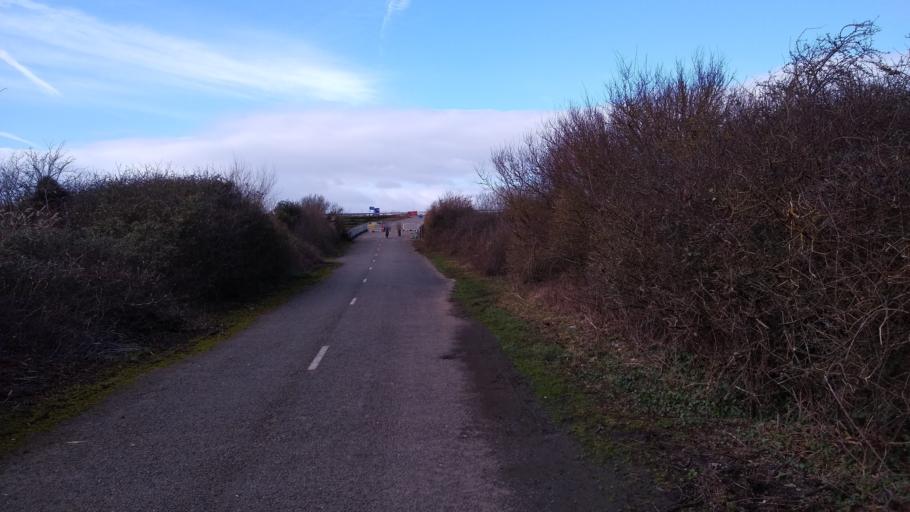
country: GB
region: England
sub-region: South Gloucestershire
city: Severn Beach
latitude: 51.5423
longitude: -2.6341
